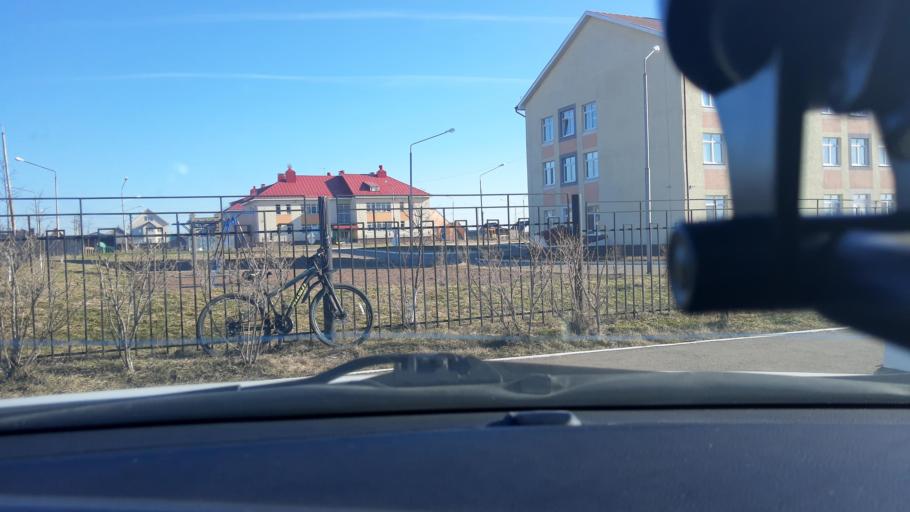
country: RU
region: Bashkortostan
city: Iglino
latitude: 54.7869
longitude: 56.2695
